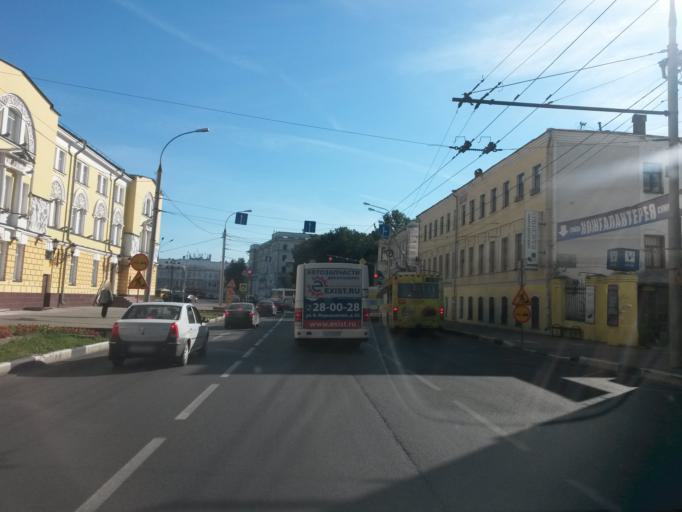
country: RU
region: Jaroslavl
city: Yaroslavl
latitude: 57.6275
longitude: 39.8844
